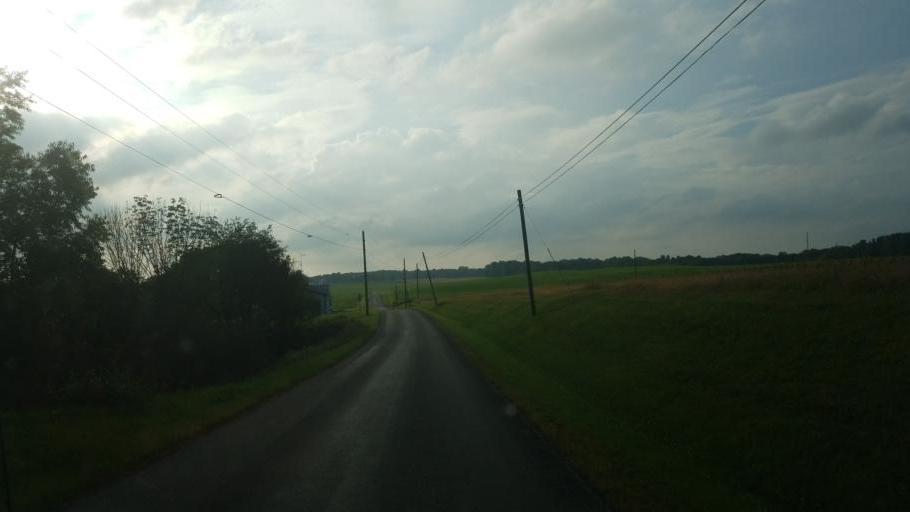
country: US
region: Ohio
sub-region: Wayne County
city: Wooster
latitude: 40.8260
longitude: -82.0413
